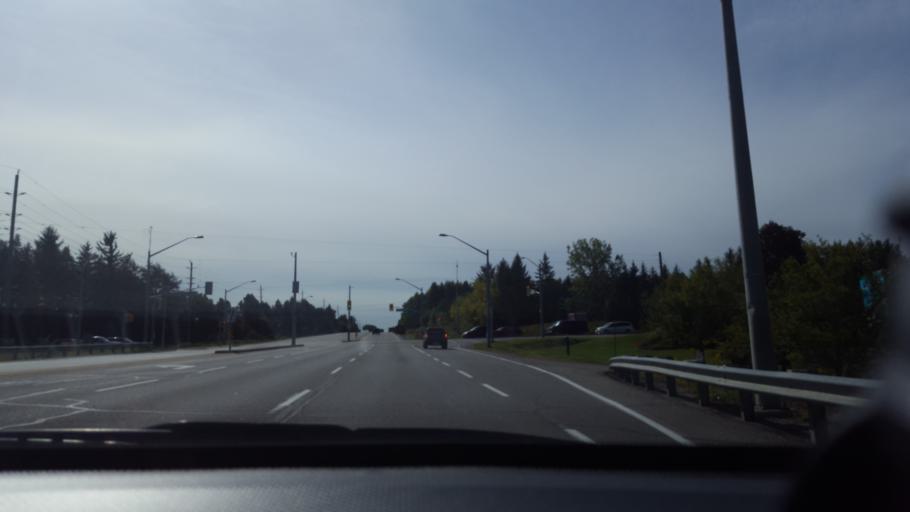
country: CA
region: Ontario
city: Newmarket
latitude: 43.9948
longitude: -79.4946
